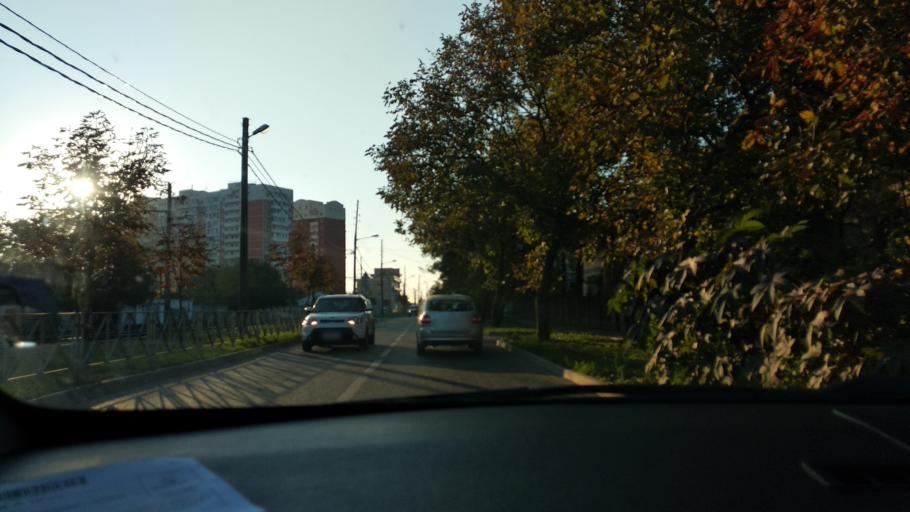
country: RU
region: Krasnodarskiy
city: Krasnodar
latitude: 45.0061
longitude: 39.0171
